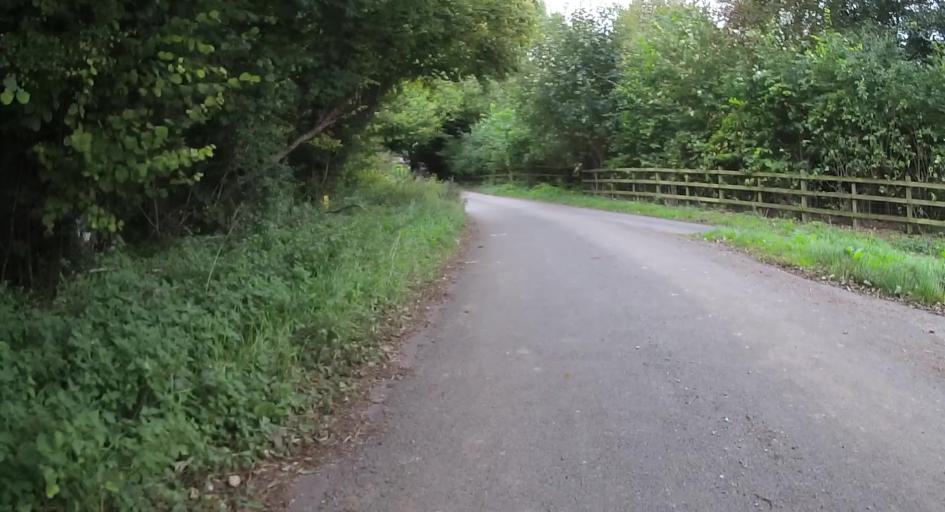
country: GB
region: England
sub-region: Hampshire
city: Four Marks
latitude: 51.1107
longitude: -1.0779
